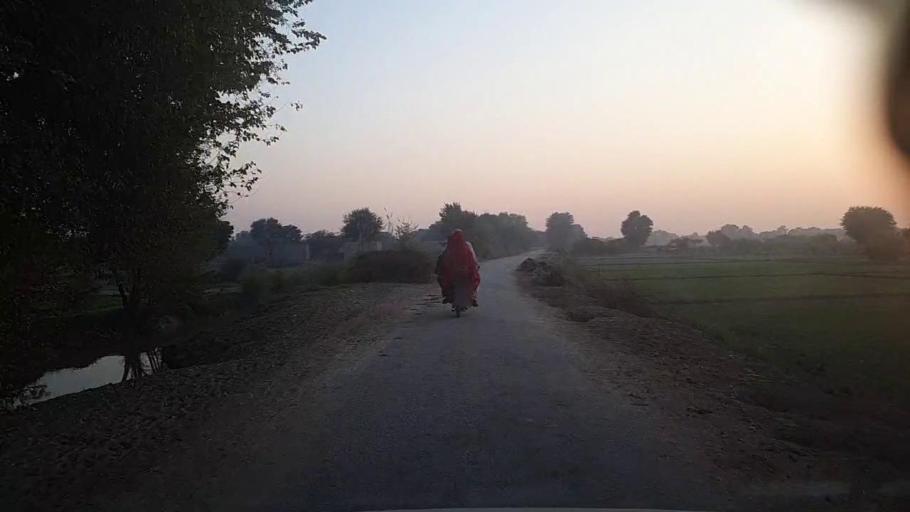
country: PK
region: Sindh
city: Karaundi
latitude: 26.8329
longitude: 68.3664
